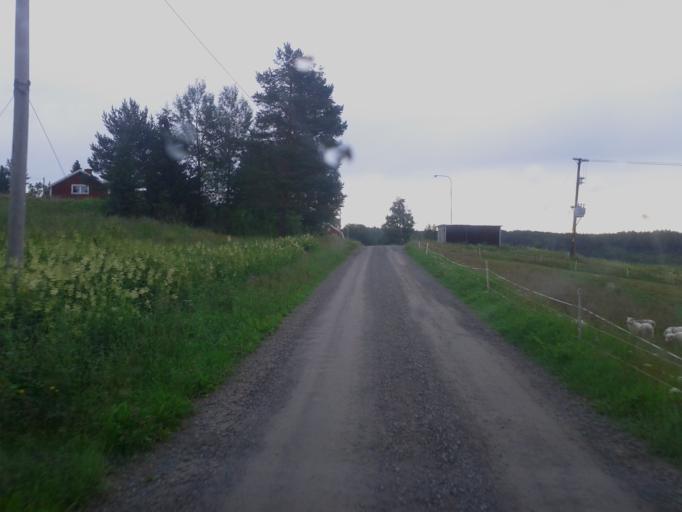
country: SE
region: Vaesternorrland
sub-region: OErnskoeldsviks Kommun
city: Bjasta
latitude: 63.0721
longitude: 18.4402
